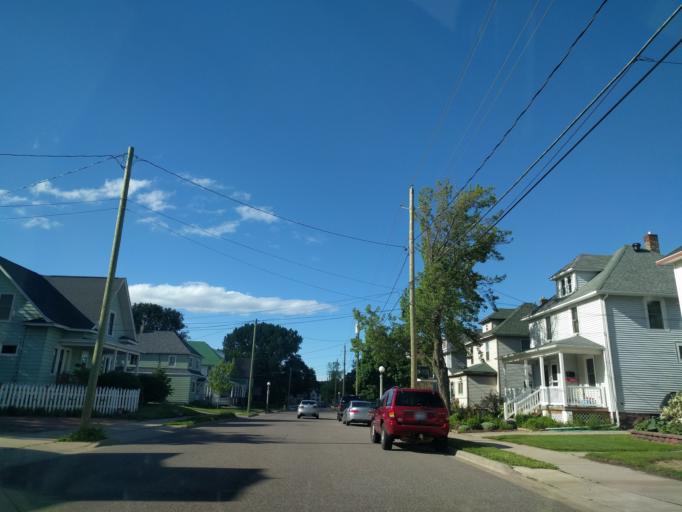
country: US
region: Michigan
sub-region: Marquette County
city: Marquette
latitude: 46.5363
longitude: -87.3967
